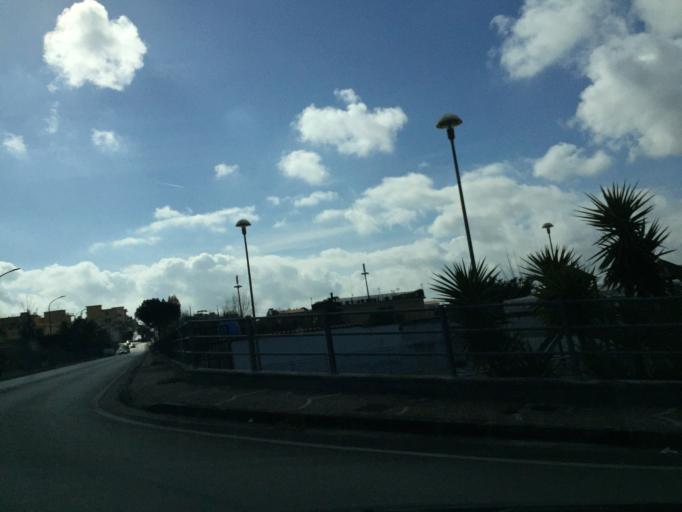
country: IT
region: Campania
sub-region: Provincia di Napoli
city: Pollena Trocchia
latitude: 40.8516
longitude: 14.3739
